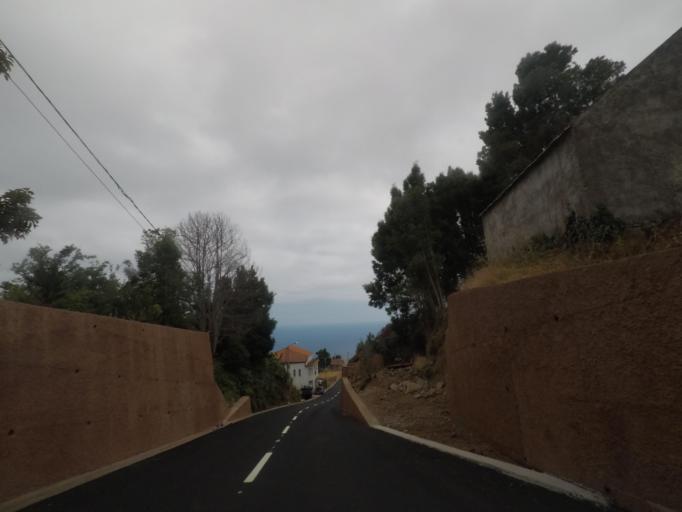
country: PT
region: Madeira
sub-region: Calheta
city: Estreito da Calheta
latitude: 32.7402
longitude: -17.1645
